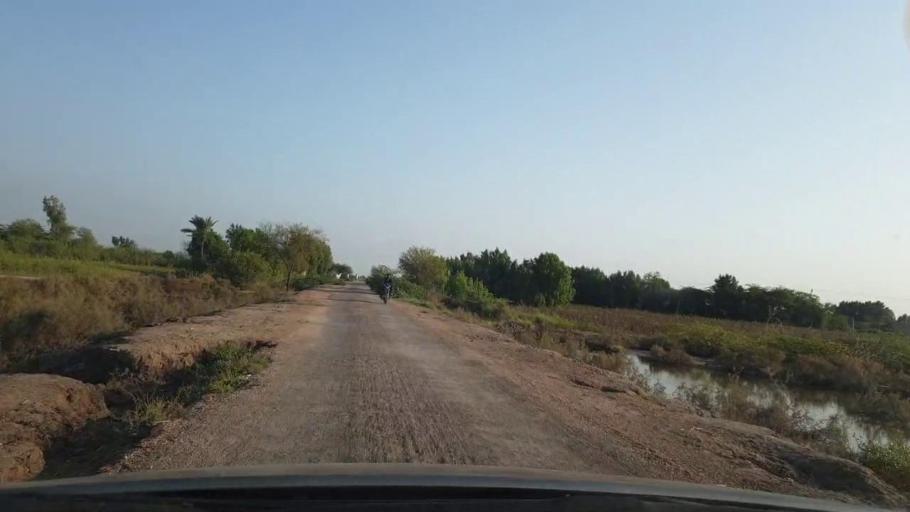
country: PK
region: Sindh
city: Naukot
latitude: 24.7632
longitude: 69.2039
